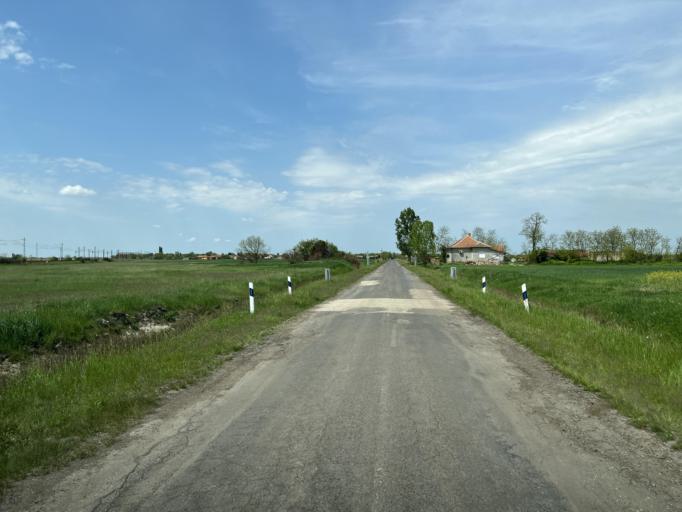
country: HU
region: Pest
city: Tapiogyorgye
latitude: 47.3203
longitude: 19.9676
